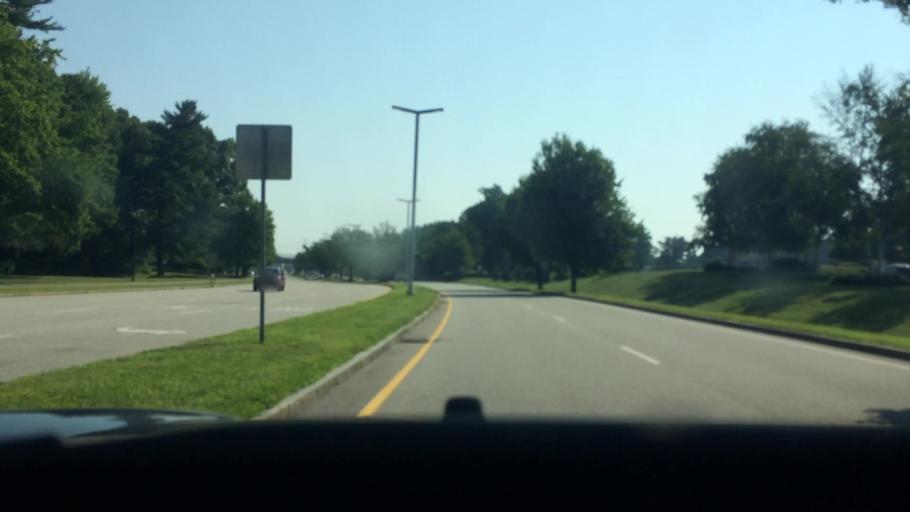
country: US
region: Maine
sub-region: York County
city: South Eliot
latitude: 43.0884
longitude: -70.8070
